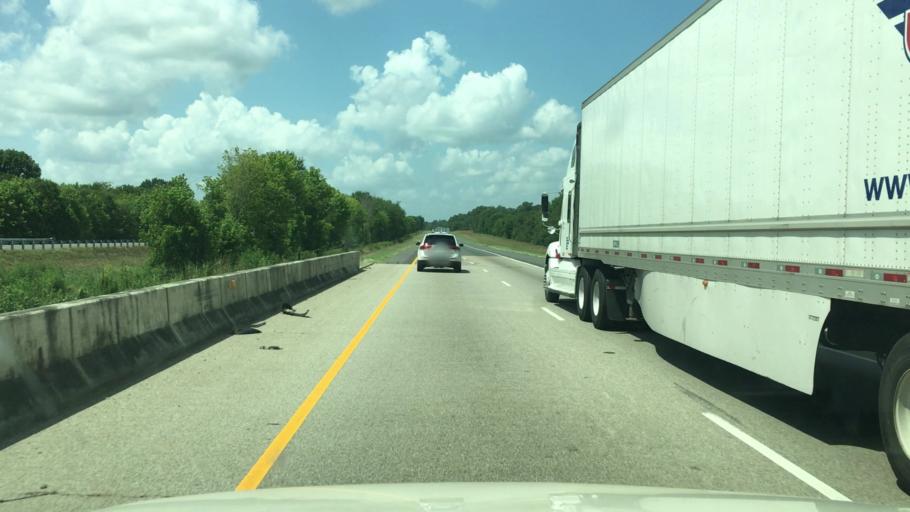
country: US
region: Arkansas
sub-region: Hempstead County
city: Hope
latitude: 33.7257
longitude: -93.5457
